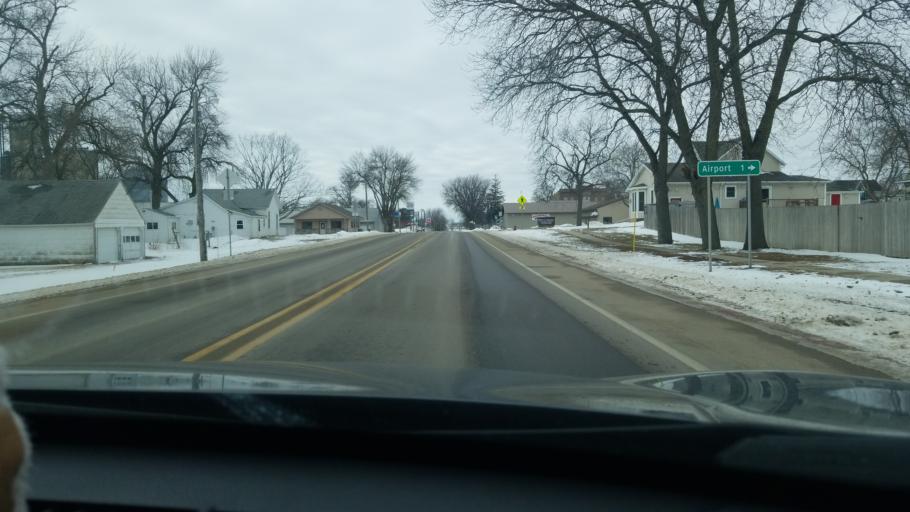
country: US
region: South Dakota
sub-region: Minnehaha County
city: Brandon
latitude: 43.4530
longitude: -96.4317
